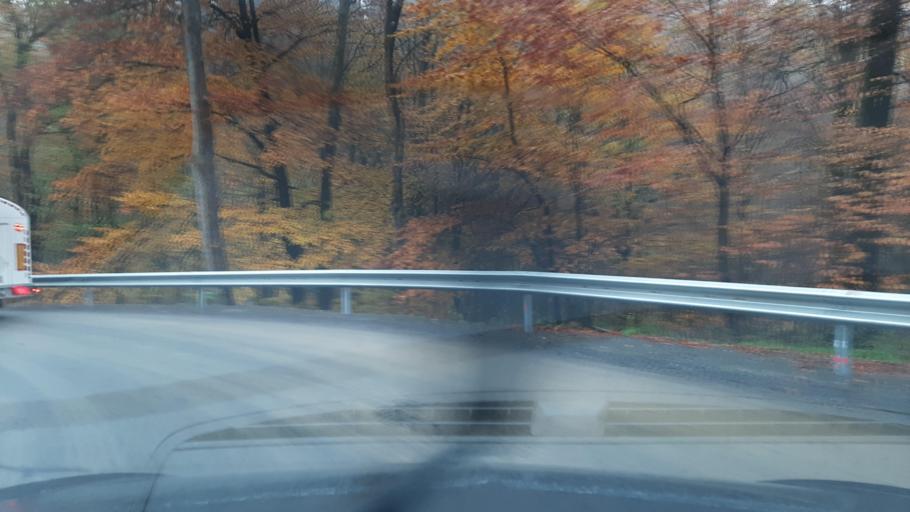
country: DE
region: North Rhine-Westphalia
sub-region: Regierungsbezirk Arnsberg
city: Bad Fredeburg
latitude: 51.2047
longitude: 8.3128
